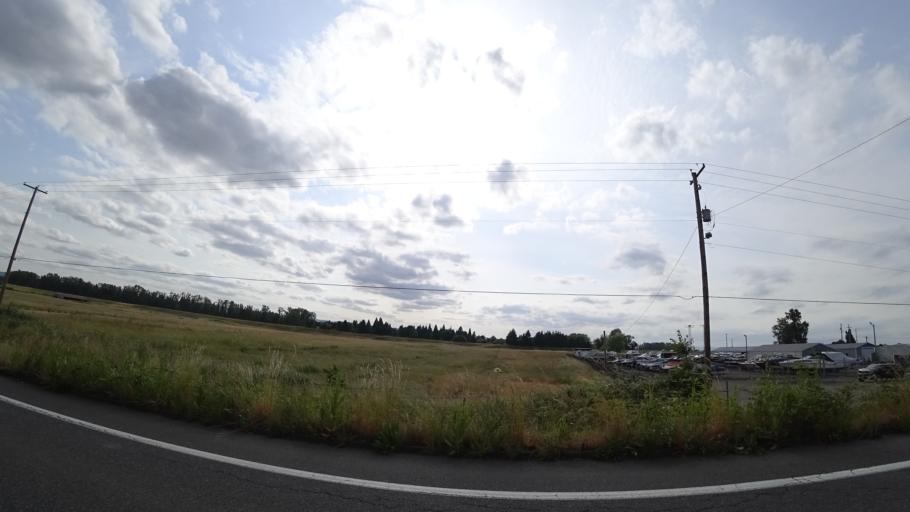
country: US
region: Washington
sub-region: Clark County
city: Vancouver
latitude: 45.5990
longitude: -122.6354
